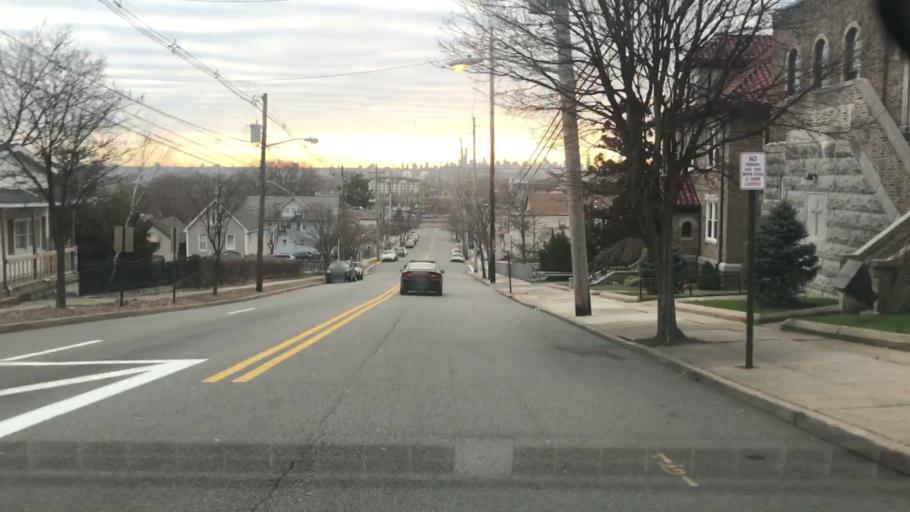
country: US
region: New Jersey
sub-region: Bergen County
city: East Rutherford
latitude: 40.8355
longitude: -74.0923
